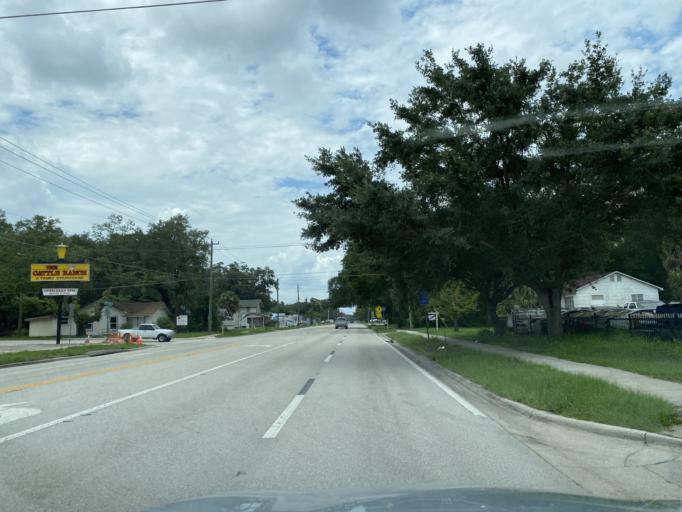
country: US
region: Florida
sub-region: Seminole County
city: Sanford
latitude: 28.7781
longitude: -81.2647
